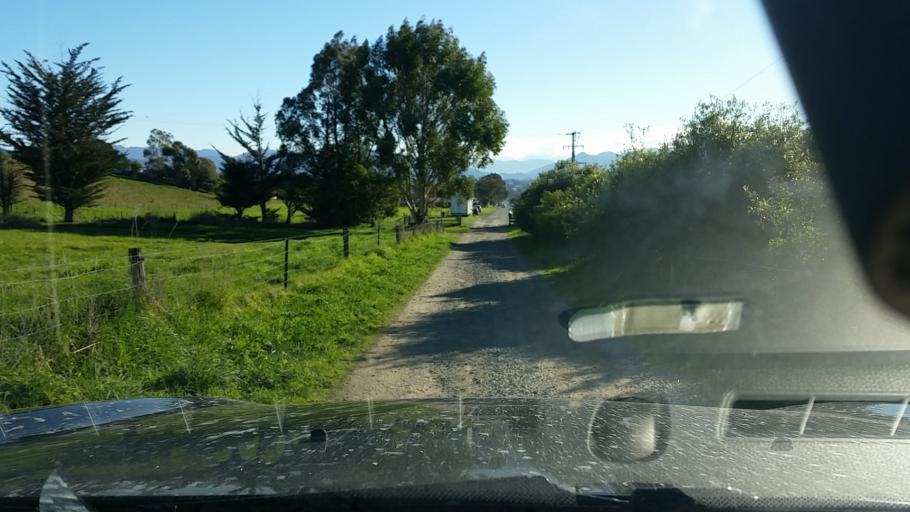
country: NZ
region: Marlborough
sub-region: Marlborough District
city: Blenheim
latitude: -41.5441
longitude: 173.9628
